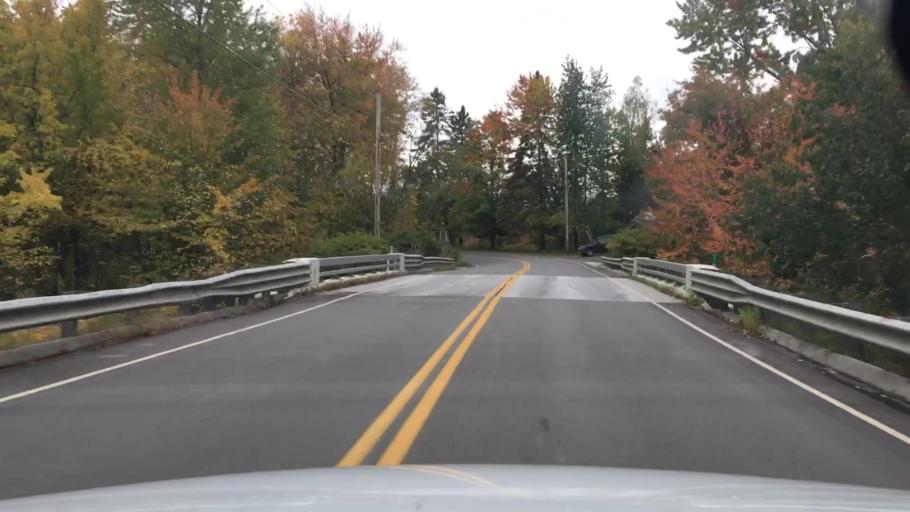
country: US
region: Maine
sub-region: Penobscot County
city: Hudson
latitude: 44.9864
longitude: -68.7774
